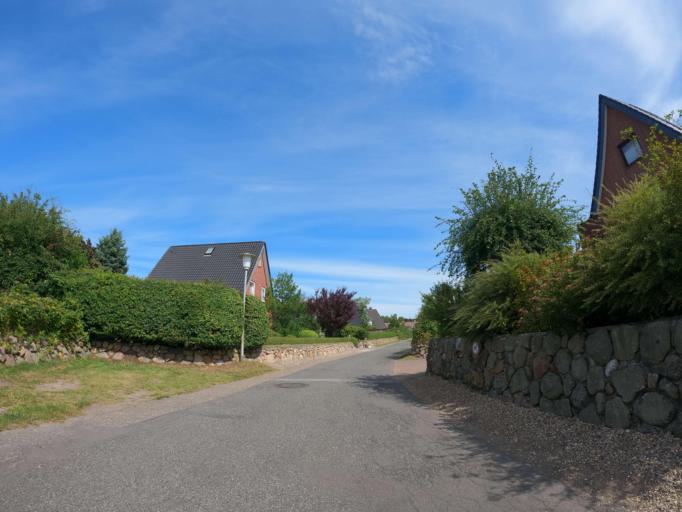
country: DE
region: Schleswig-Holstein
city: Westerland
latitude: 54.9231
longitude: 8.3205
